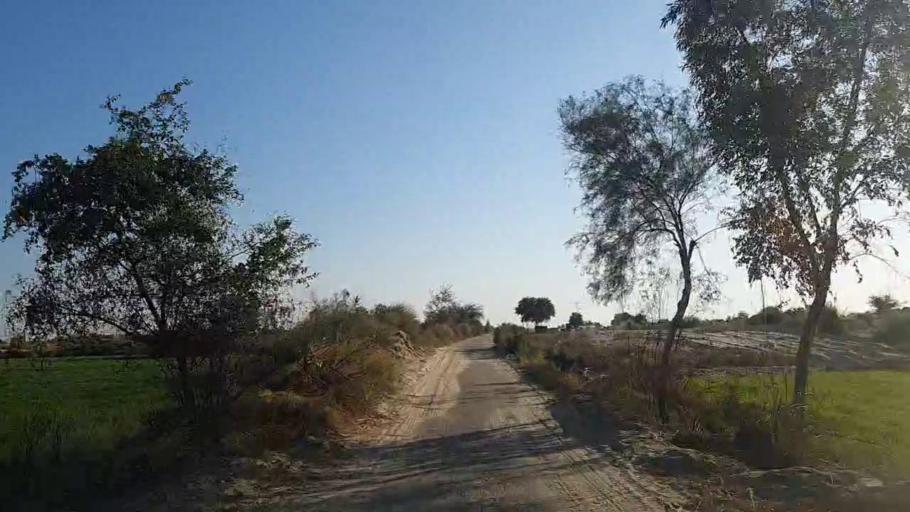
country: PK
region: Sindh
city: Khadro
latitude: 26.2732
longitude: 68.8604
